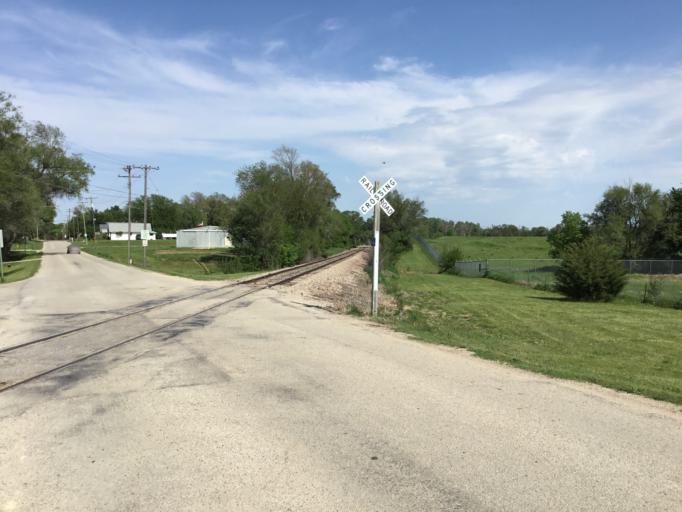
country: US
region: Kansas
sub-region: Mitchell County
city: Beloit
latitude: 39.4593
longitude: -98.1234
